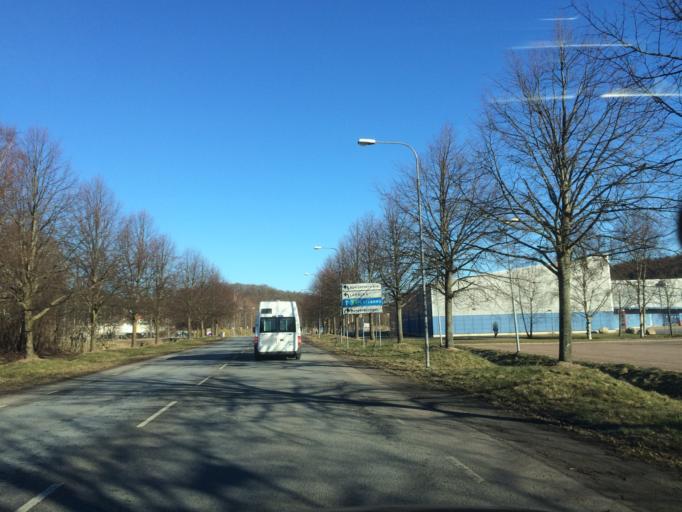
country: SE
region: Vaestra Goetaland
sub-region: Molndal
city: Kallered
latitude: 57.6083
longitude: 12.0436
